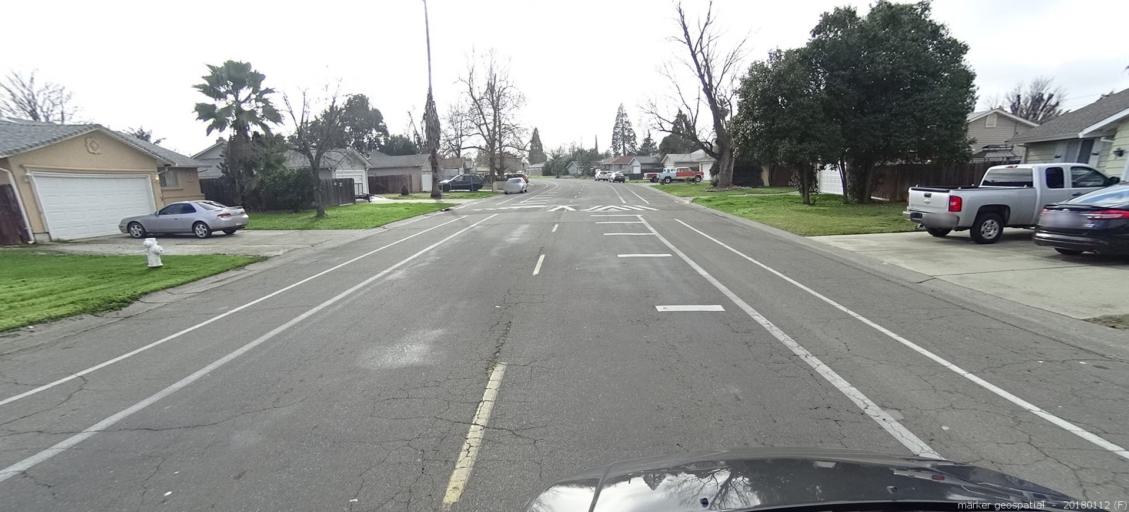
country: US
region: California
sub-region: Sacramento County
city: Rancho Cordova
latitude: 38.5976
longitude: -121.2950
